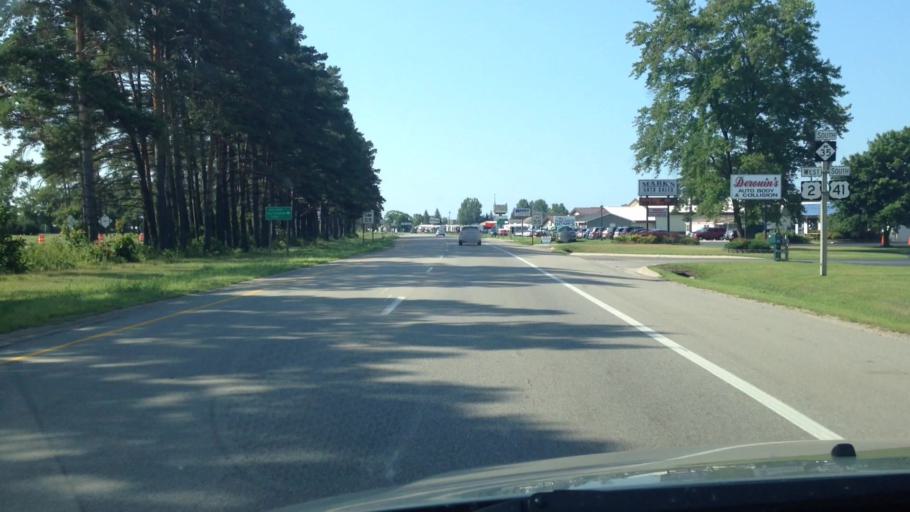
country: US
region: Michigan
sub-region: Delta County
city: Escanaba
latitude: 45.7874
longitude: -87.0823
